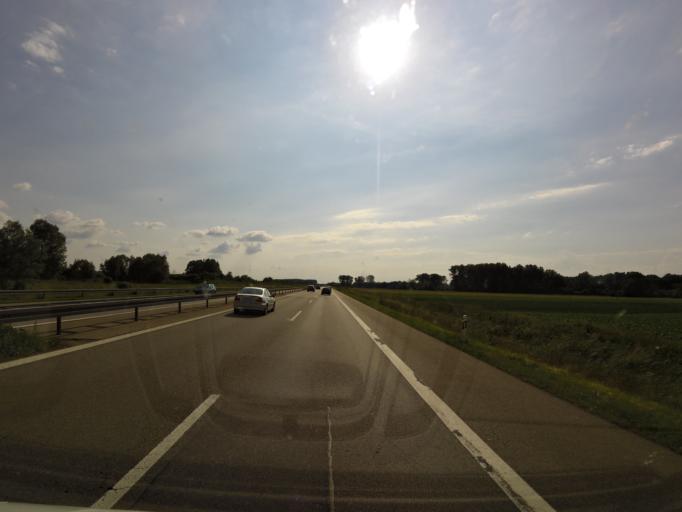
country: DE
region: Bavaria
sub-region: Lower Bavaria
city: Mamming
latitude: 48.6784
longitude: 12.5904
